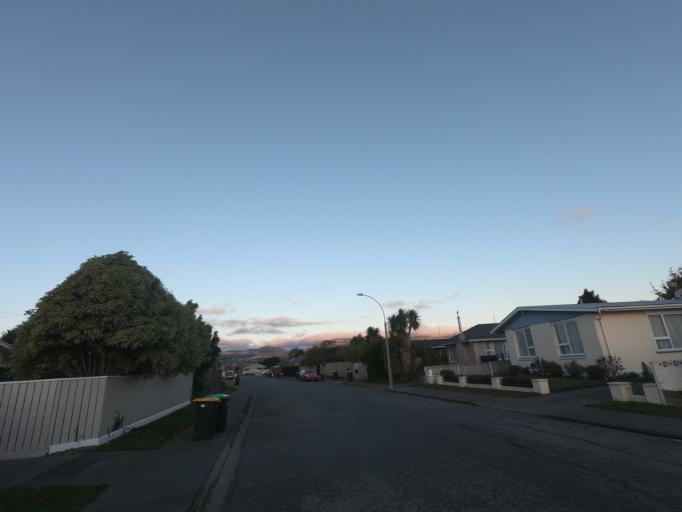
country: NZ
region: Canterbury
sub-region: Selwyn District
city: Prebbleton
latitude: -43.5743
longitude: 172.5657
